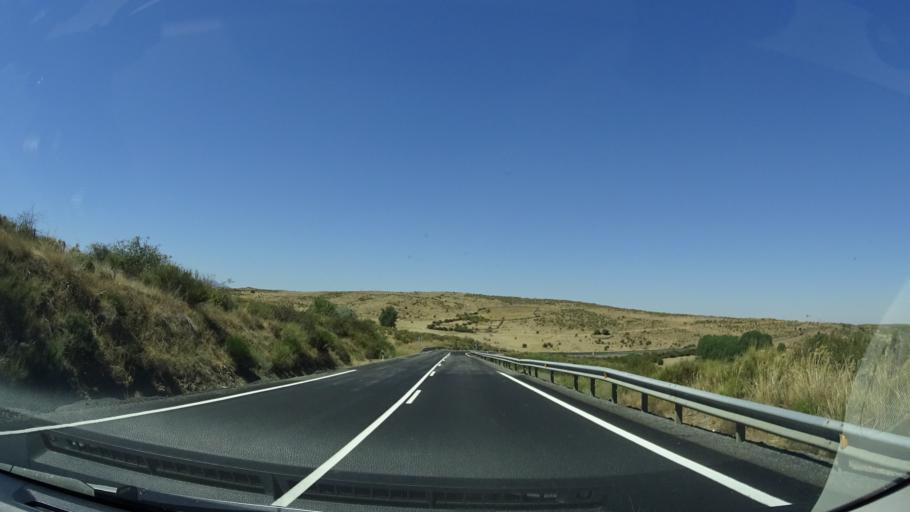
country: ES
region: Castille and Leon
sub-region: Provincia de Avila
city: Tornadizos de Avila
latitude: 40.6146
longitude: -4.5867
